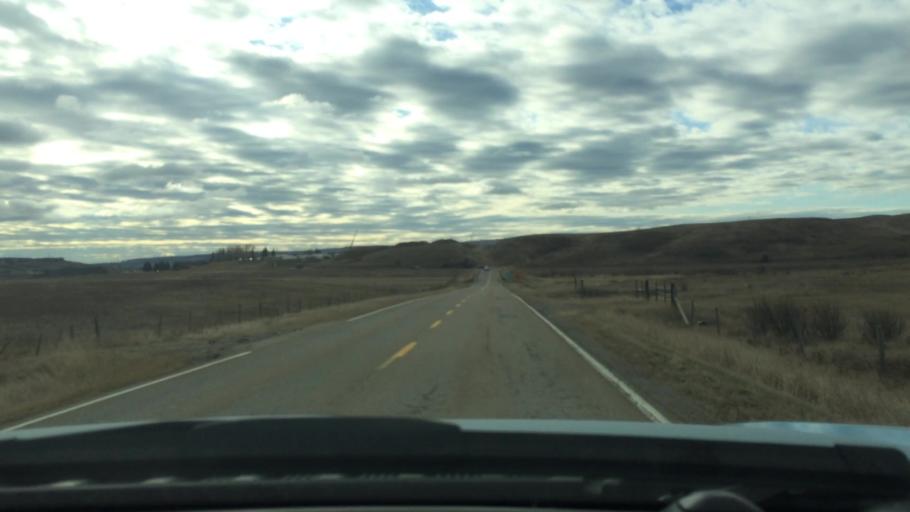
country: CA
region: Alberta
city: Airdrie
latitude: 51.1924
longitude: -114.1412
